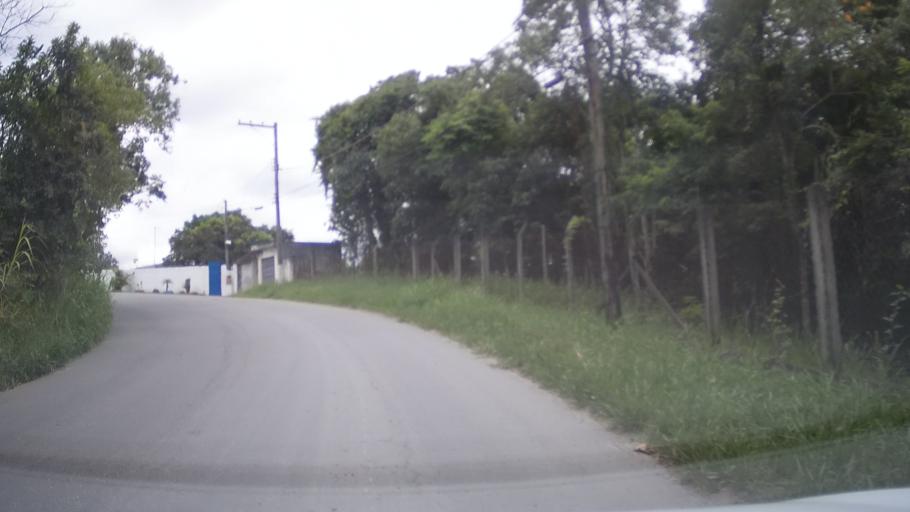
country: BR
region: Sao Paulo
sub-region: Aruja
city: Aruja
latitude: -23.3600
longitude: -46.2895
